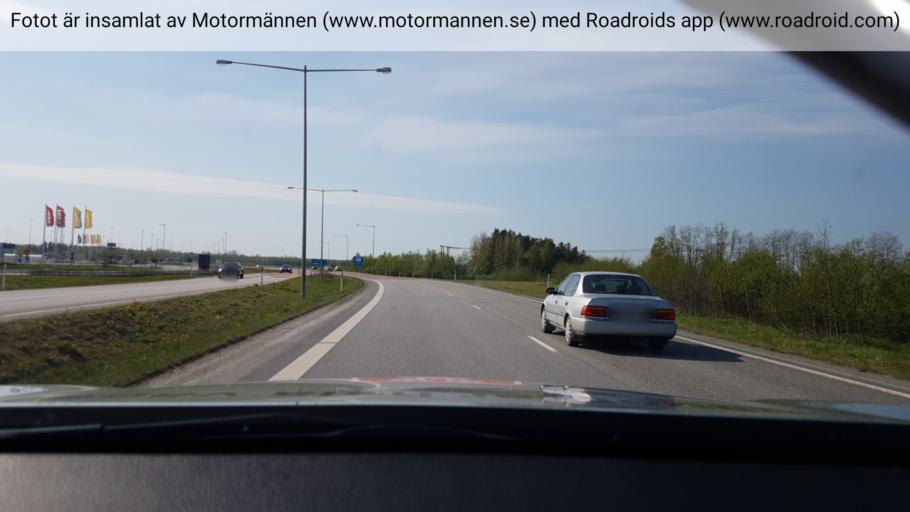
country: SE
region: Vaesterbotten
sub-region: Umea Kommun
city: Umea
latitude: 63.8100
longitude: 20.2490
